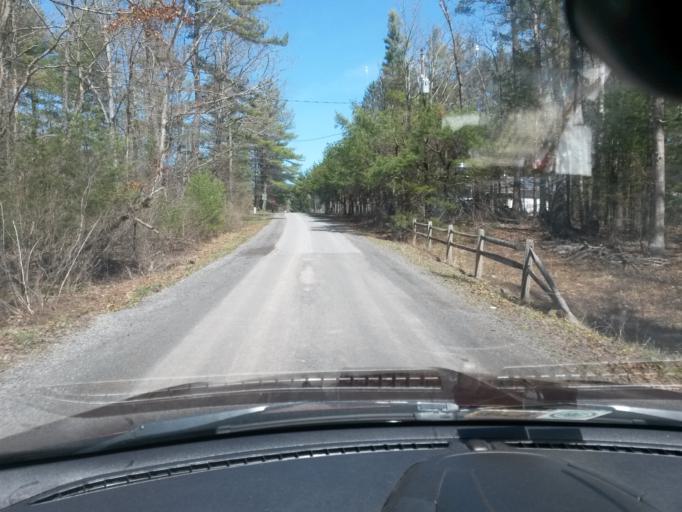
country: US
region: West Virginia
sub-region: Greenbrier County
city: Ronceverte
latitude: 37.6326
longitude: -80.3414
